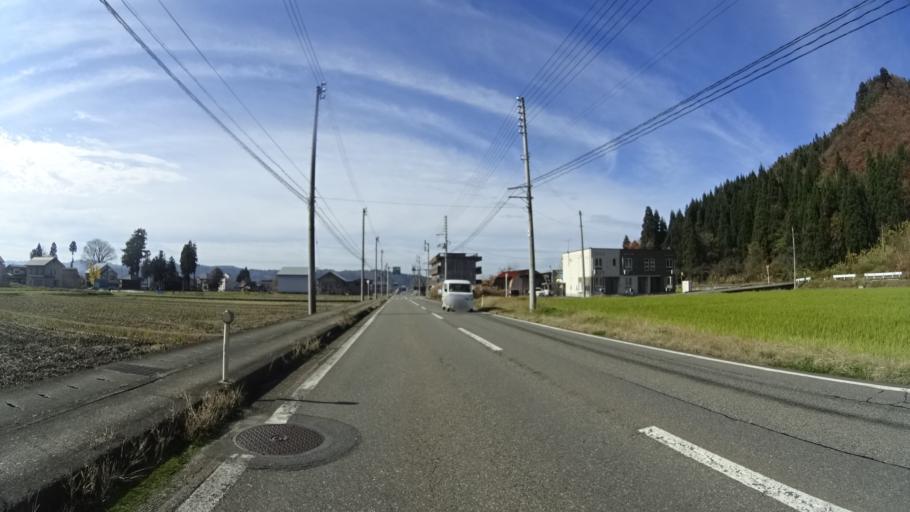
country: JP
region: Niigata
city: Muikamachi
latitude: 37.2281
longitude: 138.9900
